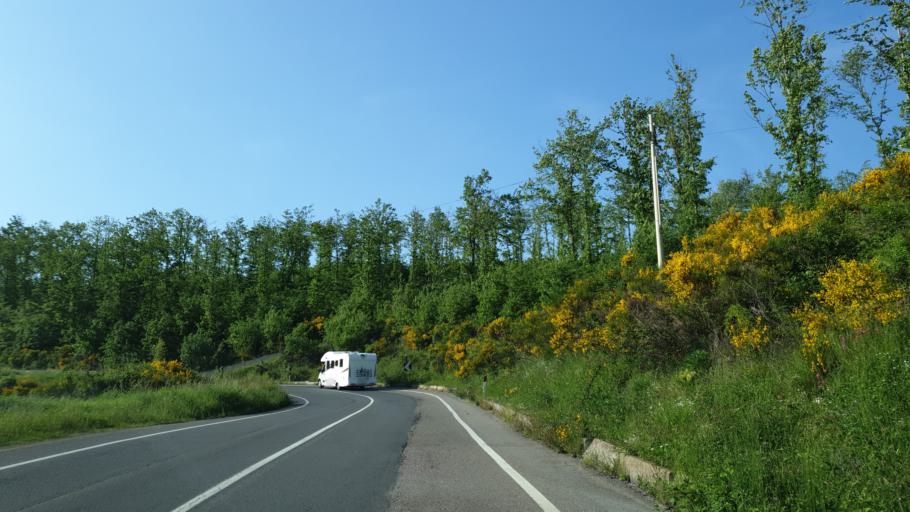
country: IT
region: Tuscany
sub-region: Province of Arezzo
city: Stia
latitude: 43.7784
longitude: 11.6785
